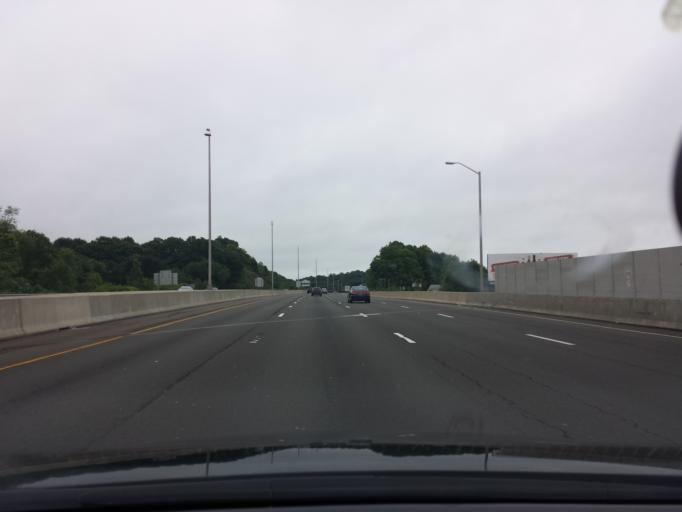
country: US
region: Connecticut
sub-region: New Haven County
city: East Haven
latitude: 41.2847
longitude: -72.8743
